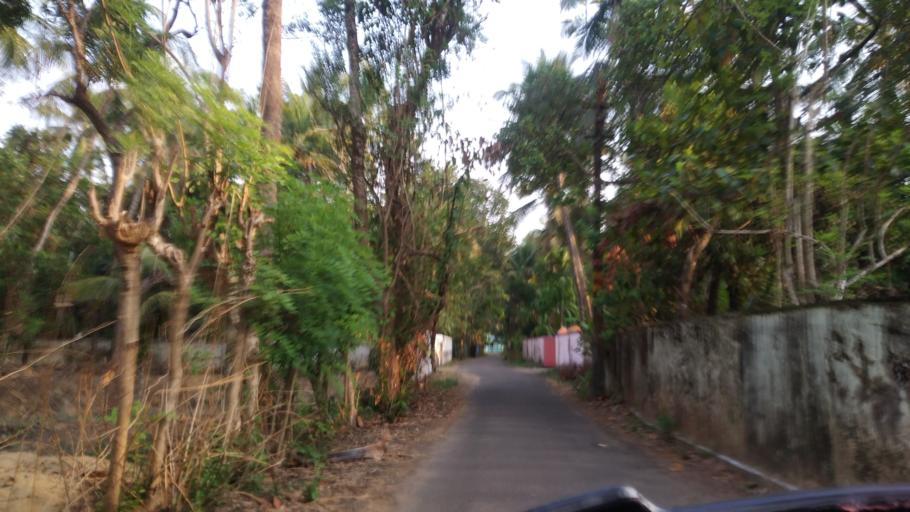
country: IN
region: Kerala
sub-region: Thrissur District
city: Thanniyam
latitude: 10.4098
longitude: 76.0892
